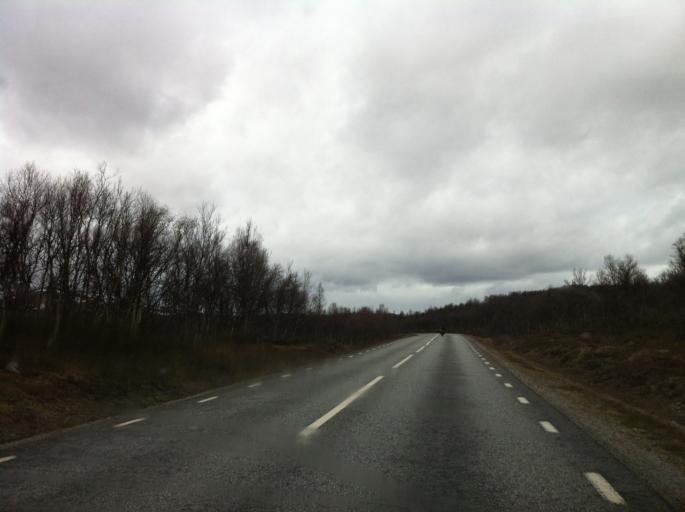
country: NO
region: Sor-Trondelag
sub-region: Tydal
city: Aas
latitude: 62.6112
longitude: 12.1528
